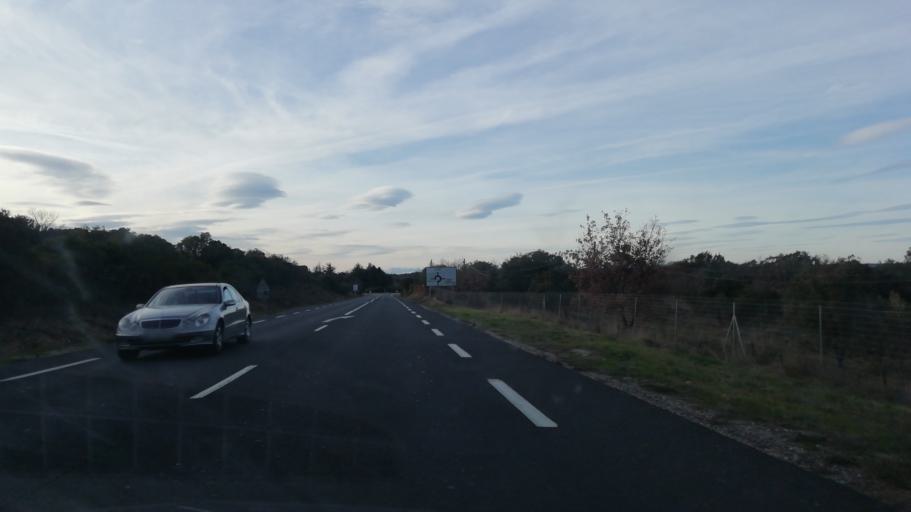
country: FR
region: Languedoc-Roussillon
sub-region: Departement du Gard
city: Clarensac
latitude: 43.8598
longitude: 4.2208
